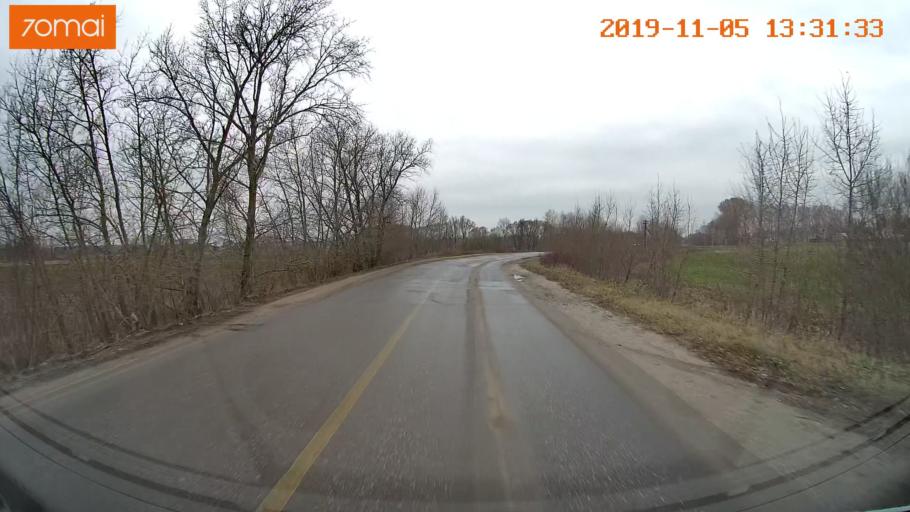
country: RU
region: Ivanovo
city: Shuya
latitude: 56.8771
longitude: 41.3936
